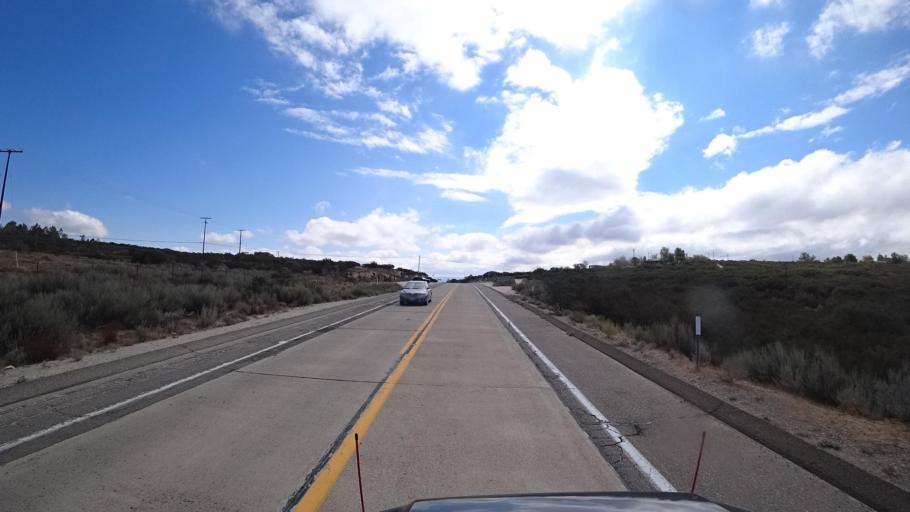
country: US
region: California
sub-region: San Diego County
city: Campo
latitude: 32.6705
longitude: -116.3168
